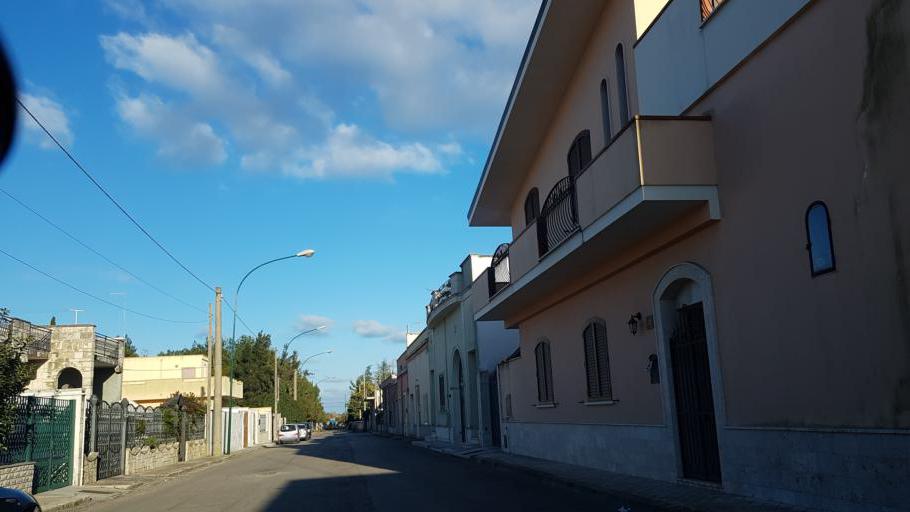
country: IT
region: Apulia
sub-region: Provincia di Lecce
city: Squinzano
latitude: 40.4428
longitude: 18.0390
